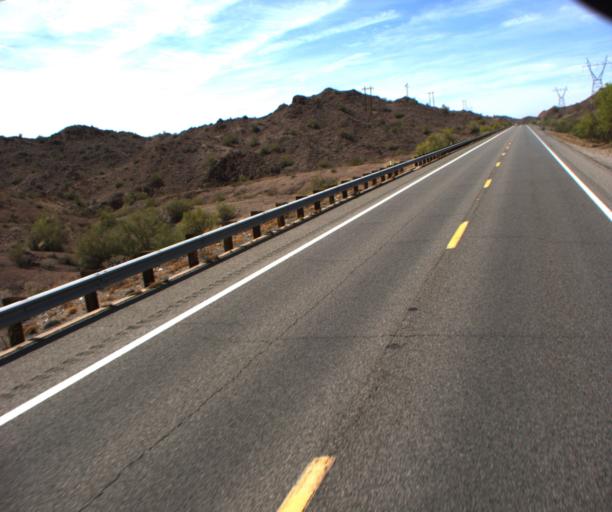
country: US
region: Arizona
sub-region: La Paz County
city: Cienega Springs
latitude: 34.3444
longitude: -114.1480
